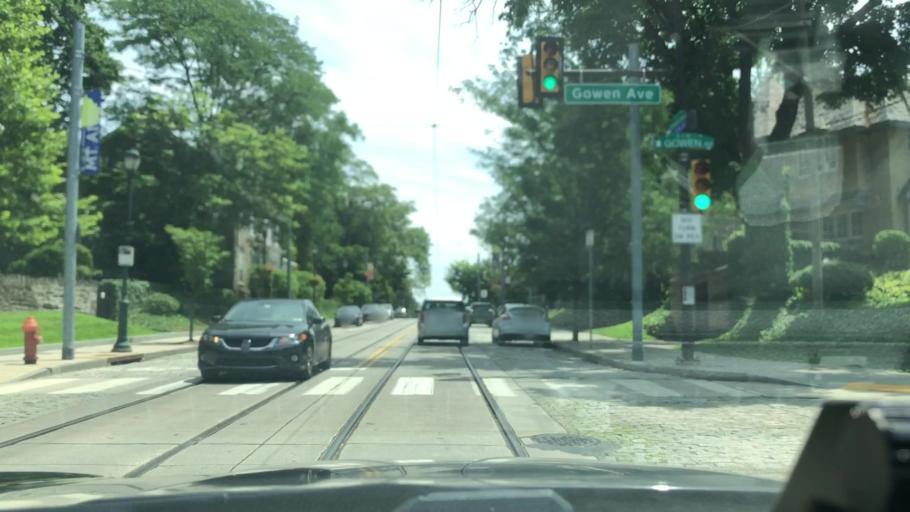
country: US
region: Pennsylvania
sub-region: Montgomery County
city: Wyndmoor
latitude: 40.0626
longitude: -75.1929
